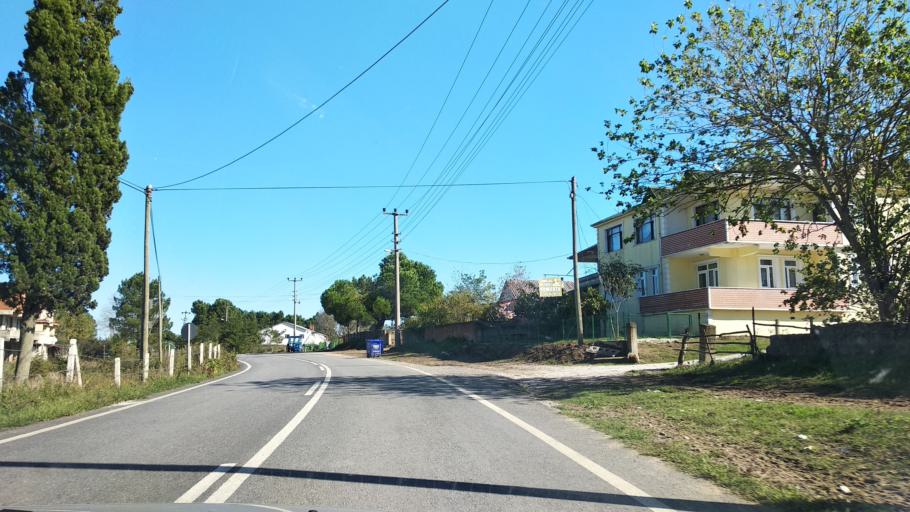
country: TR
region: Sakarya
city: Karasu
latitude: 41.1185
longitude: 30.6125
